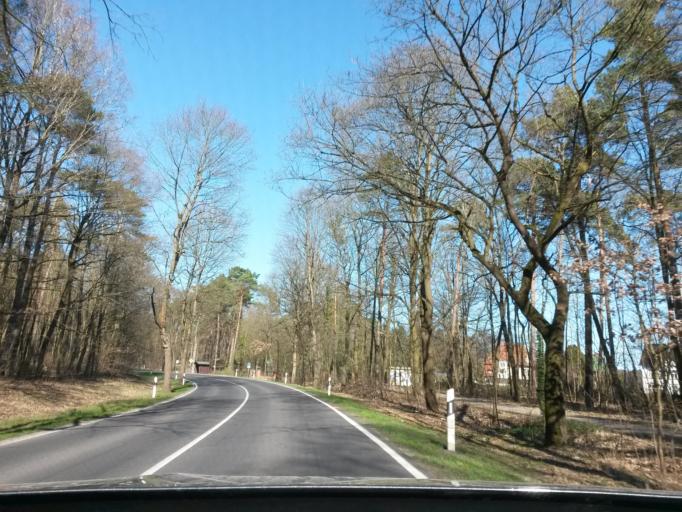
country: DE
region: Brandenburg
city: Grunheide
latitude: 52.4285
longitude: 13.8296
